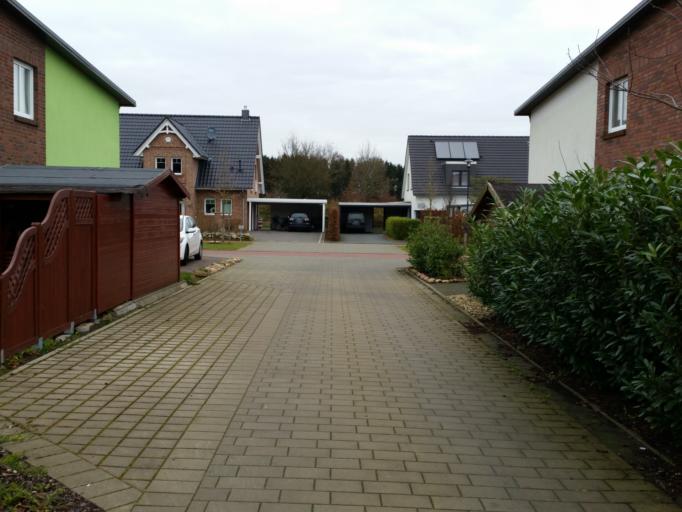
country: DE
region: Lower Saxony
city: Buchholz in der Nordheide
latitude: 53.3424
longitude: 9.8851
